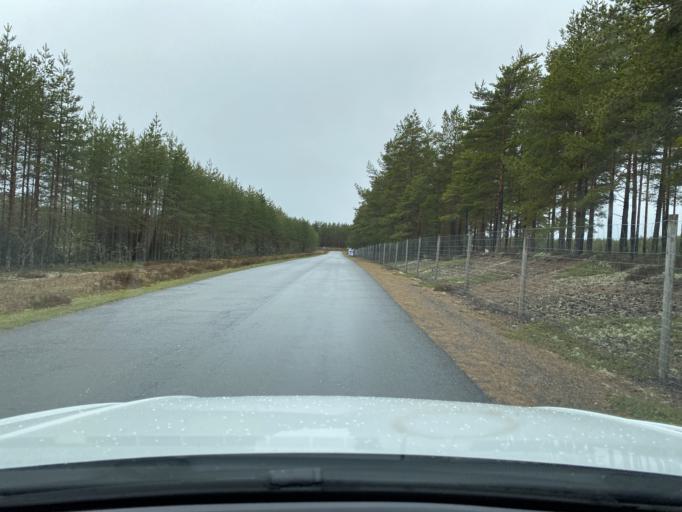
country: FI
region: Satakunta
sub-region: Pori
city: Vampula
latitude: 60.9720
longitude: 22.6643
